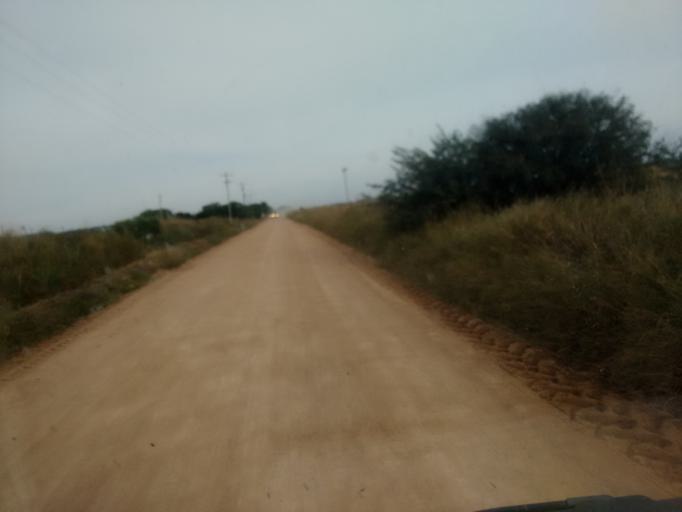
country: BR
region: Rio Grande do Sul
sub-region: Sao Lourenco Do Sul
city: Sao Lourenco do Sul
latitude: -31.1740
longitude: -51.7439
